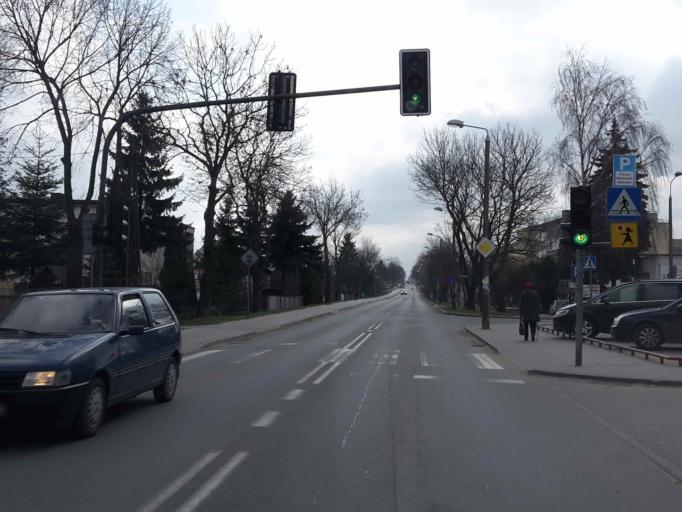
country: PL
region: Kujawsko-Pomorskie
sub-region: Powiat brodnicki
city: Brodnica
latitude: 53.2442
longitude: 19.4069
